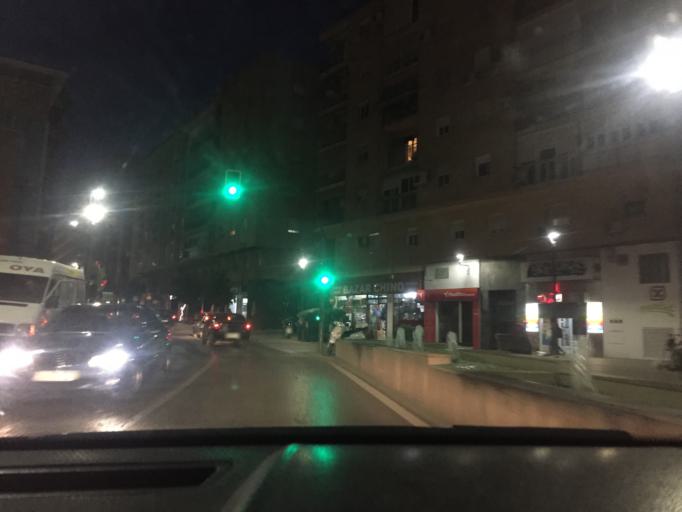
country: ES
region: Andalusia
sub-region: Provincia de Jaen
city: Jaen
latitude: 37.7783
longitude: -3.7929
